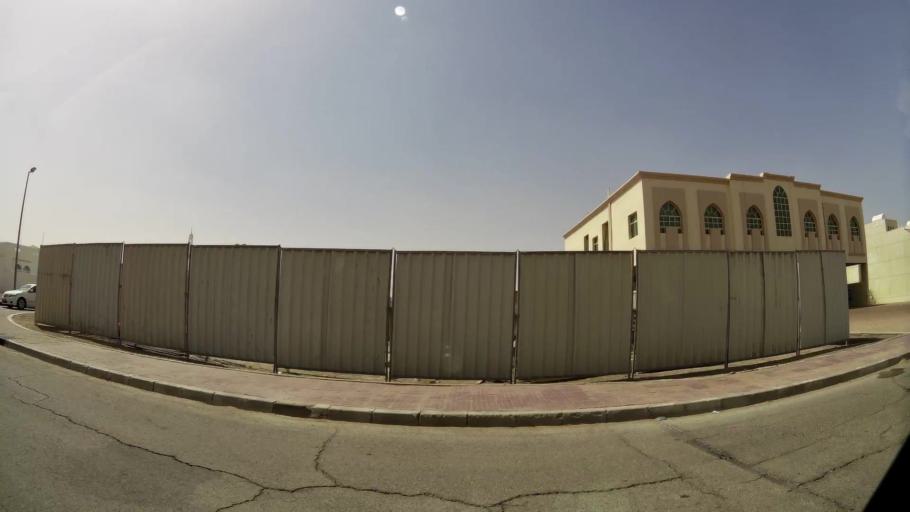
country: AE
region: Abu Dhabi
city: Al Ain
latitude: 24.2217
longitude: 55.6935
